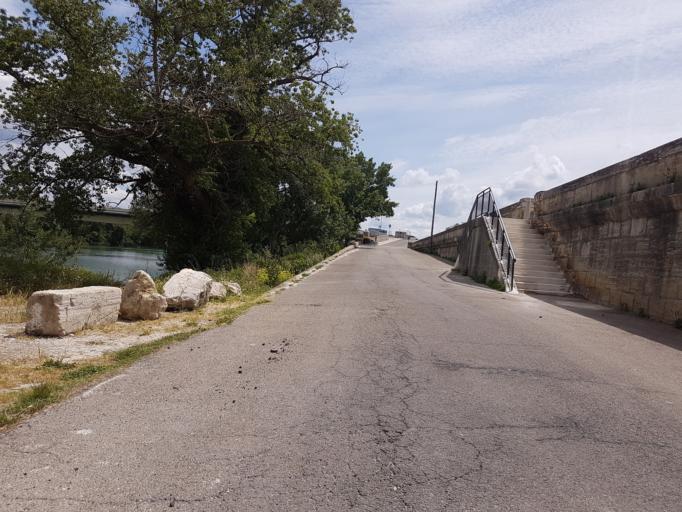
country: FR
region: Languedoc-Roussillon
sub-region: Departement du Gard
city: Beaucaire
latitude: 43.8060
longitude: 4.6487
